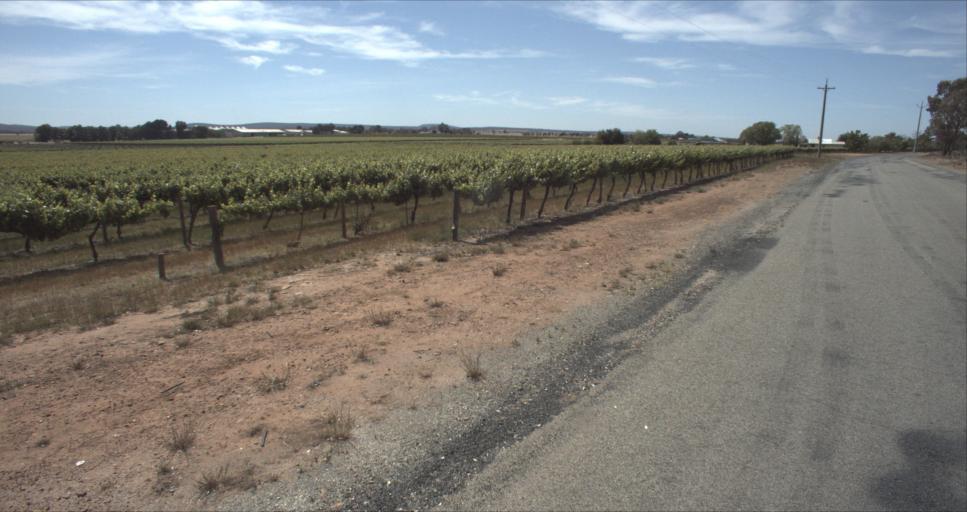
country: AU
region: New South Wales
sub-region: Leeton
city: Leeton
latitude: -34.5602
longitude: 146.4582
